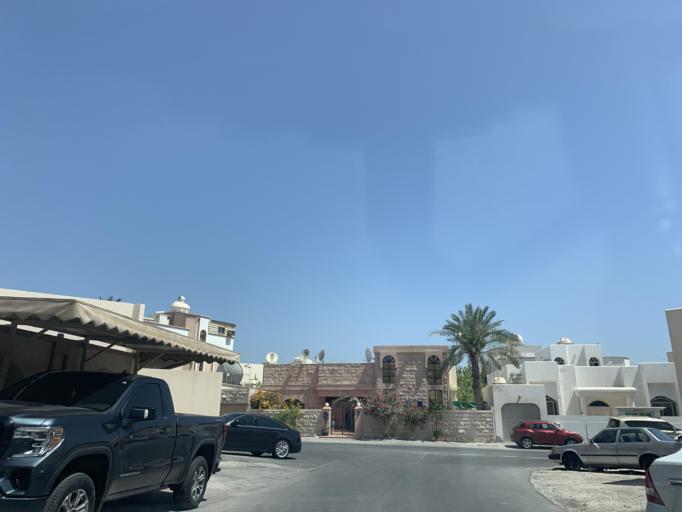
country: BH
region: Northern
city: Ar Rifa'
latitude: 26.1333
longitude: 50.5795
